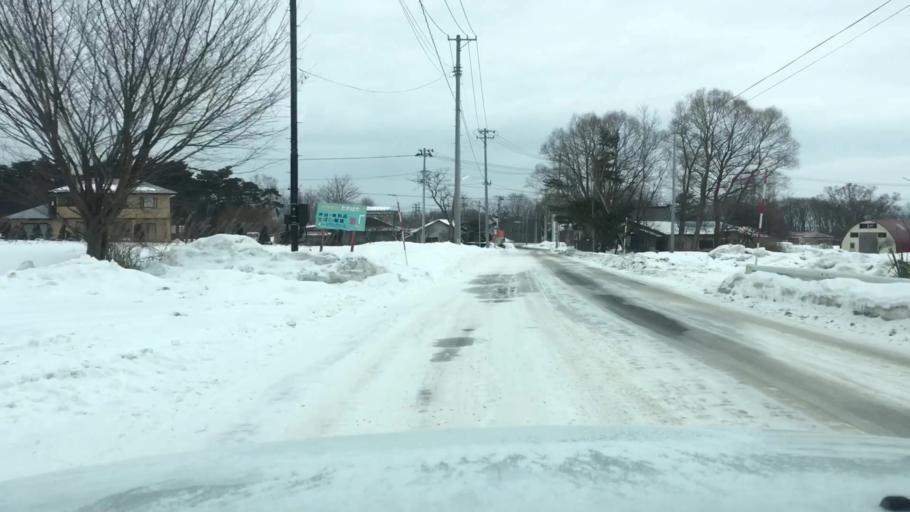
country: JP
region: Iwate
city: Shizukuishi
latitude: 39.9147
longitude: 141.0053
